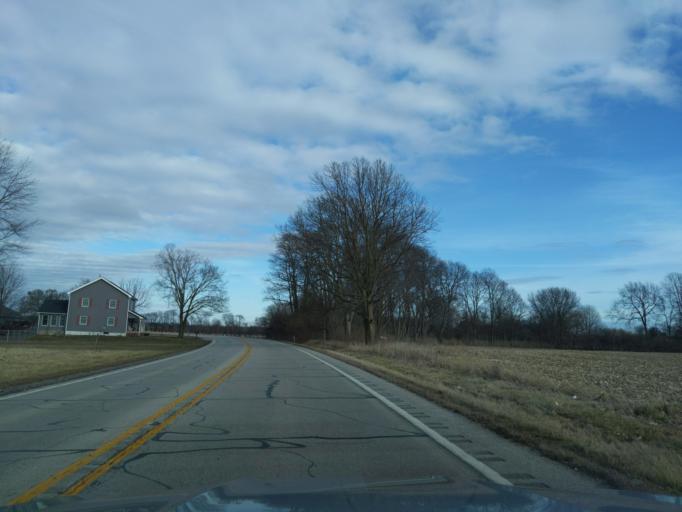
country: US
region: Indiana
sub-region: Tippecanoe County
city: Shadeland
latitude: 40.3594
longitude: -86.9726
